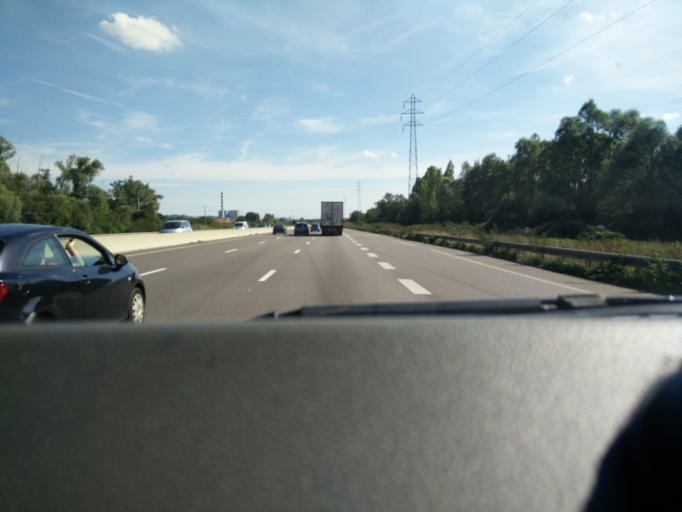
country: FR
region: Lorraine
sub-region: Departement de la Moselle
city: Argancy
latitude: 49.1779
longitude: 6.1780
